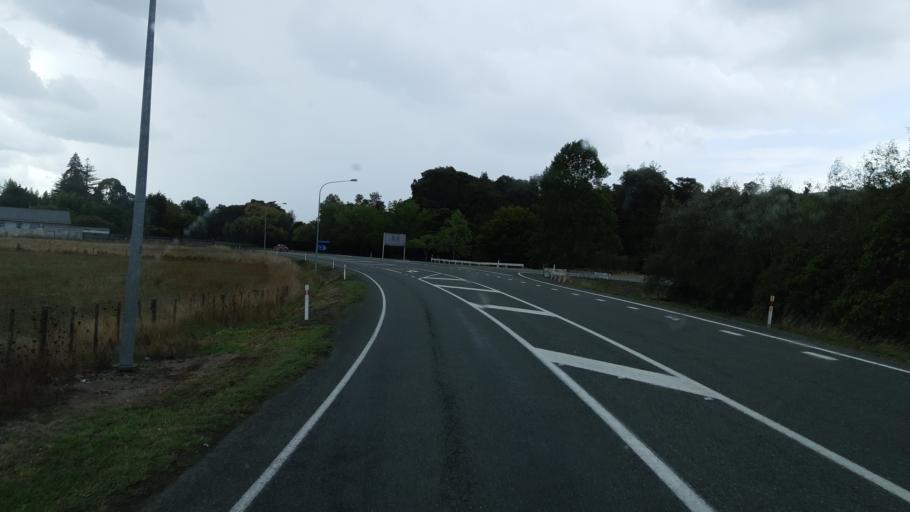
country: NZ
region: Tasman
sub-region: Tasman District
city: Wakefield
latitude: -41.4085
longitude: 173.0359
